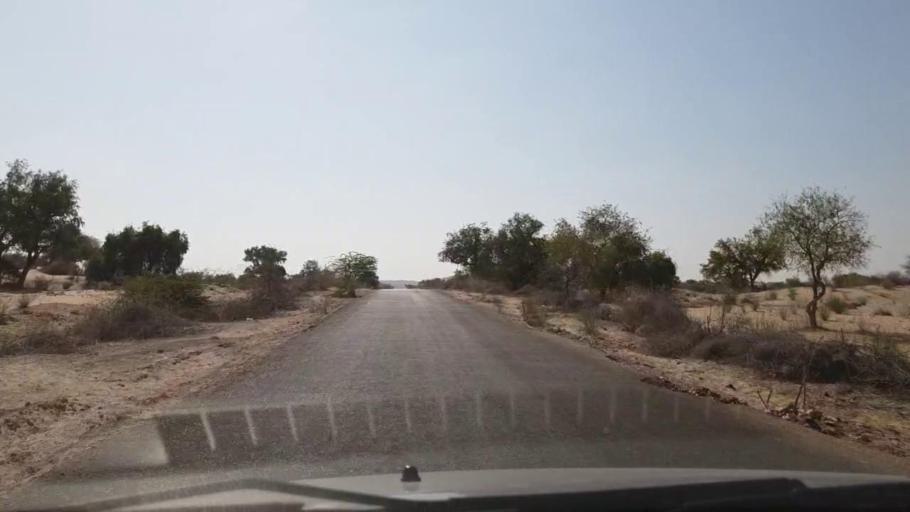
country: PK
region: Sindh
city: Mithi
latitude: 24.6590
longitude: 69.7561
